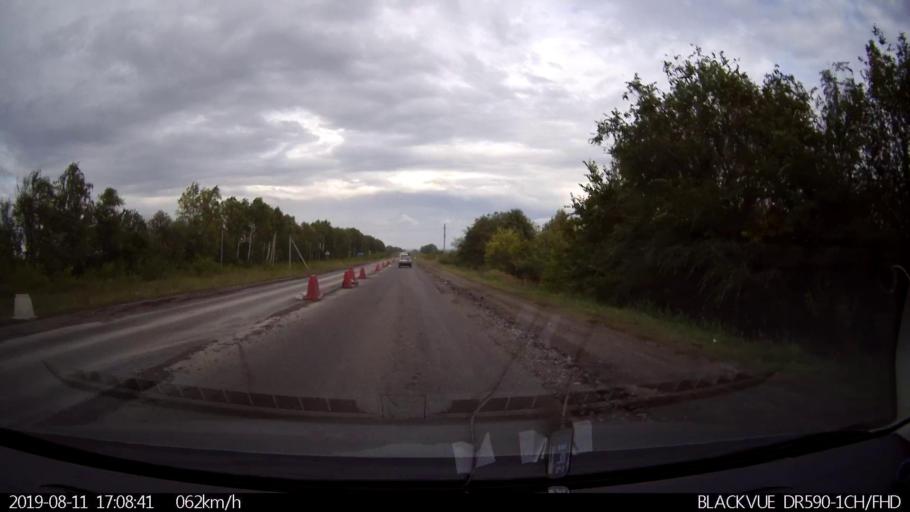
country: RU
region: Ulyanovsk
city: Mayna
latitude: 54.2934
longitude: 47.8439
